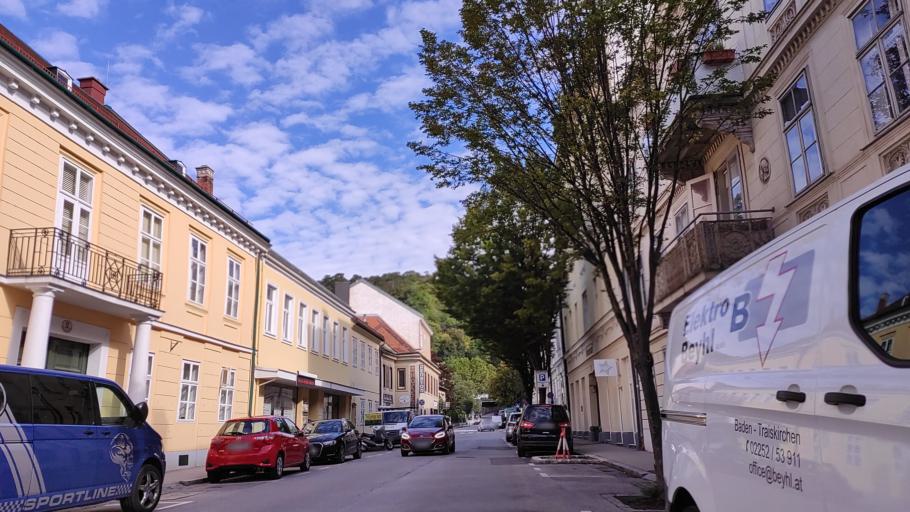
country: AT
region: Lower Austria
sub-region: Politischer Bezirk Baden
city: Baden
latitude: 48.0083
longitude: 16.2317
